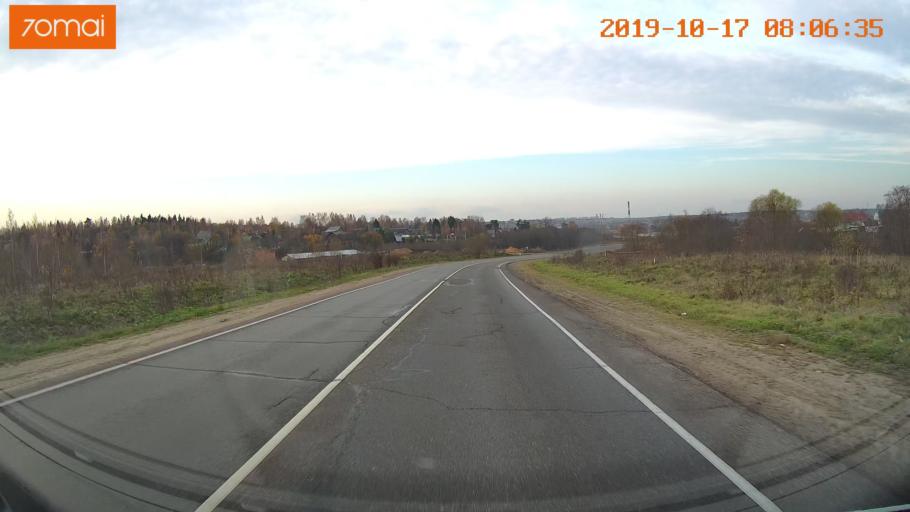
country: RU
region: Vladimir
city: Kol'chugino
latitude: 56.3209
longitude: 39.4123
